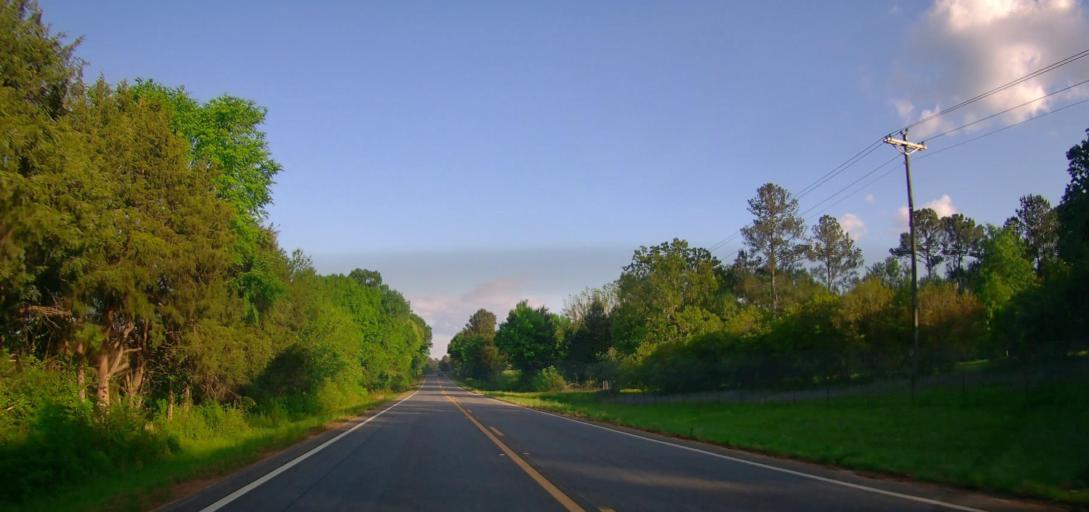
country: US
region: Georgia
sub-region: Putnam County
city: Eatonton
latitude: 33.3326
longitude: -83.5066
